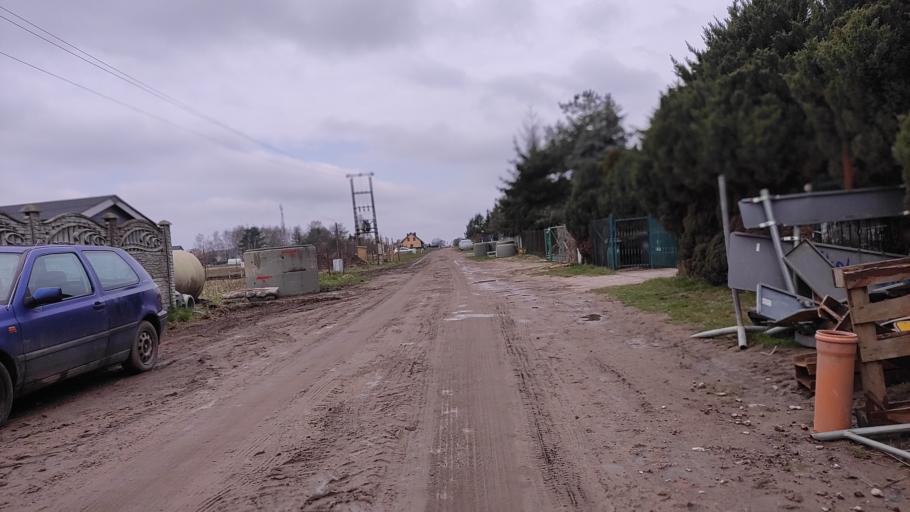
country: PL
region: Greater Poland Voivodeship
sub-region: Powiat poznanski
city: Kostrzyn
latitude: 52.4039
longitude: 17.1729
